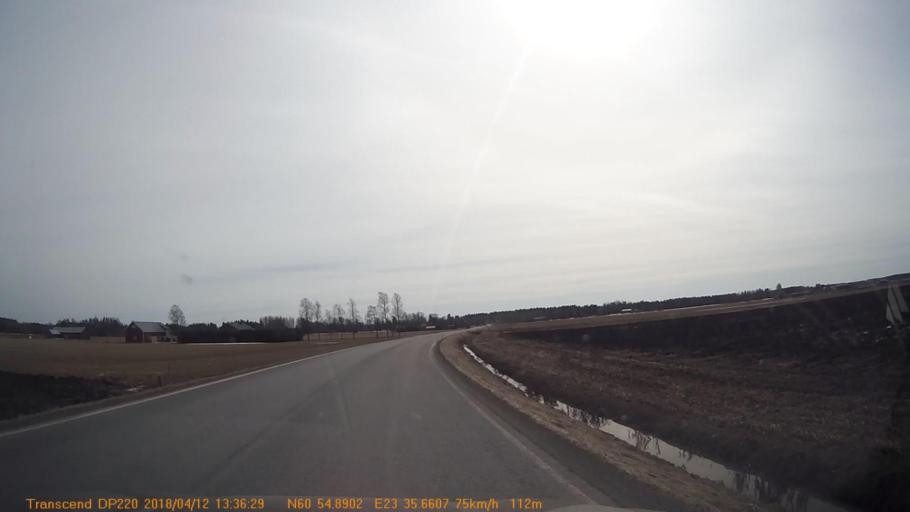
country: FI
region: Haeme
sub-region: Forssa
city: Forssa
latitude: 60.9145
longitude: 23.5944
